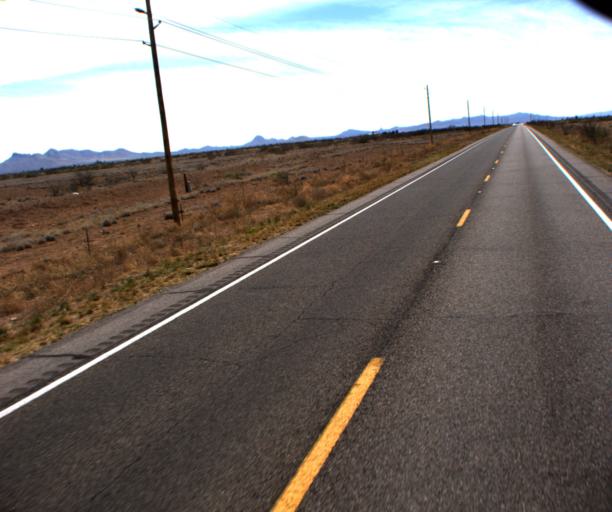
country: US
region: Arizona
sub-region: Cochise County
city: Pirtleville
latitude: 31.4299
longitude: -109.5857
